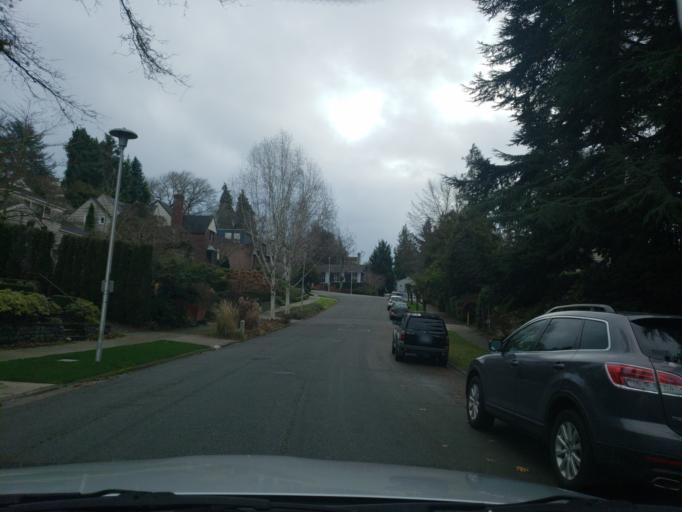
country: US
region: Washington
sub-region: King County
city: Medina
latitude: 47.6532
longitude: -122.2799
